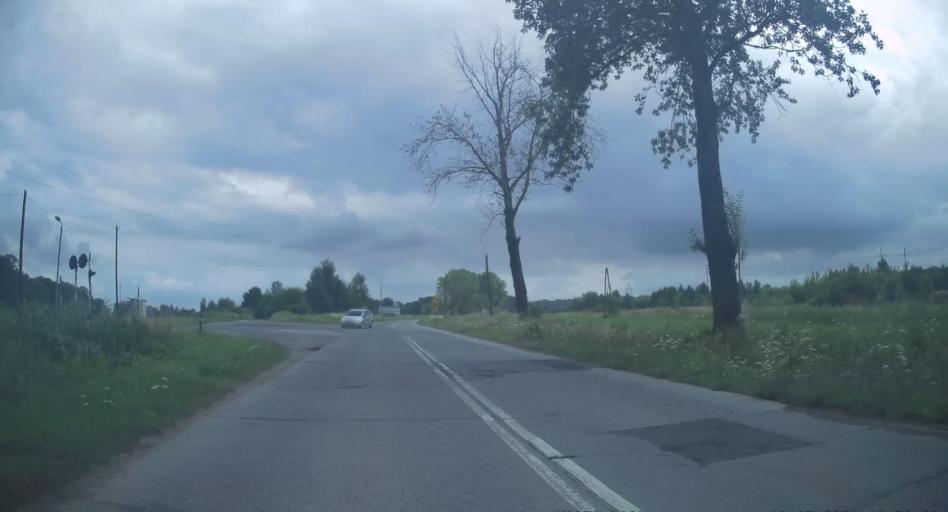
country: PL
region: Opole Voivodeship
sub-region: Powiat nyski
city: Paczkow
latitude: 50.4792
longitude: 16.9993
